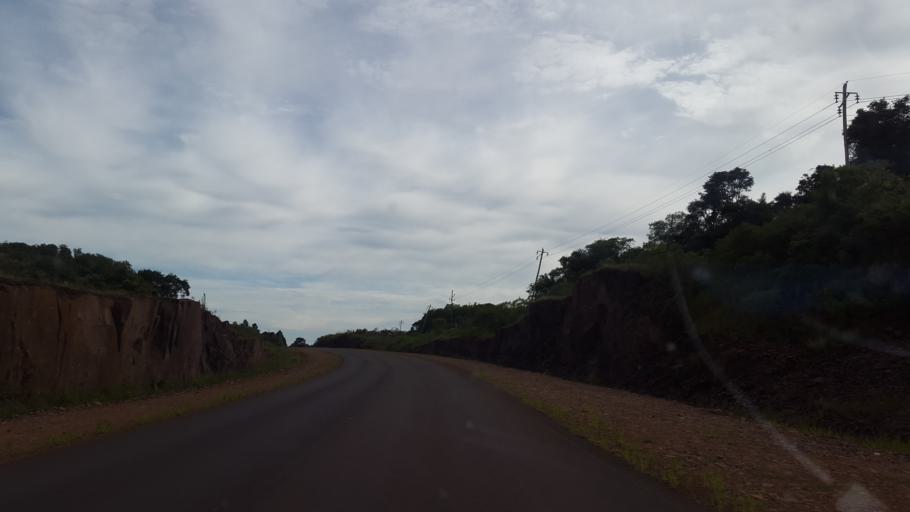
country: AR
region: Misiones
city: Bernardo de Irigoyen
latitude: -26.4332
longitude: -53.8534
